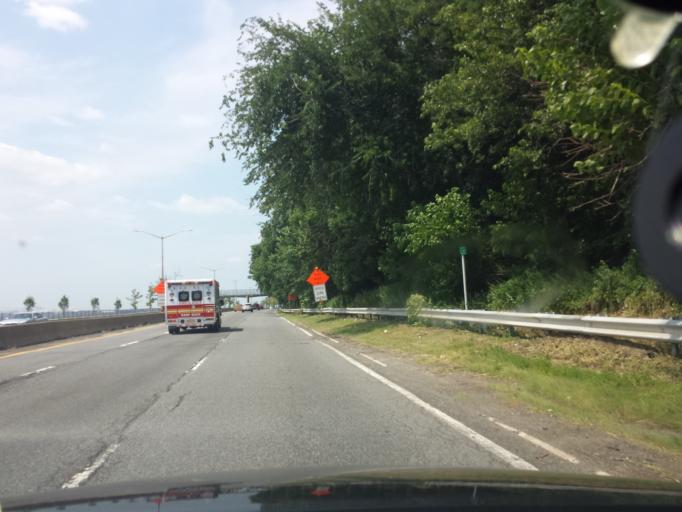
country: US
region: New York
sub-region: Kings County
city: Bensonhurst
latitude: 40.6186
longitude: -74.0407
